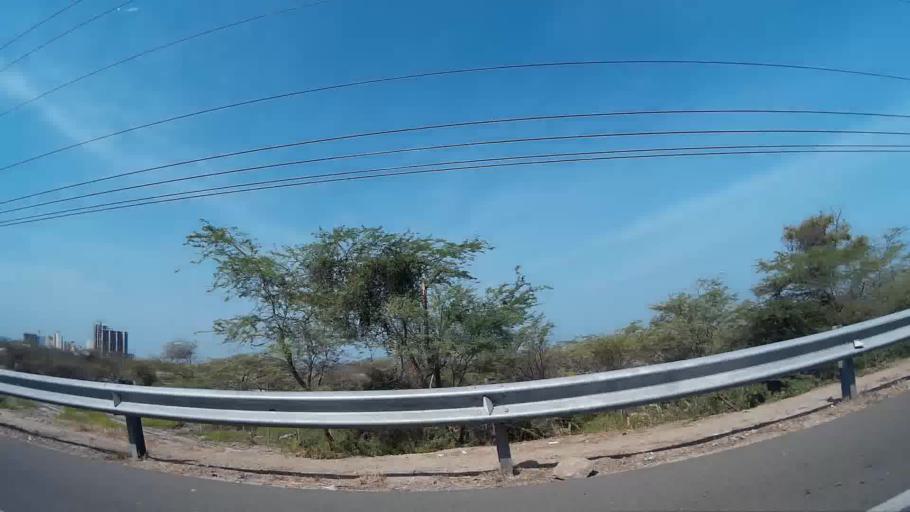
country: CO
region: Magdalena
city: Santa Marta
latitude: 11.1628
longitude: -74.2268
